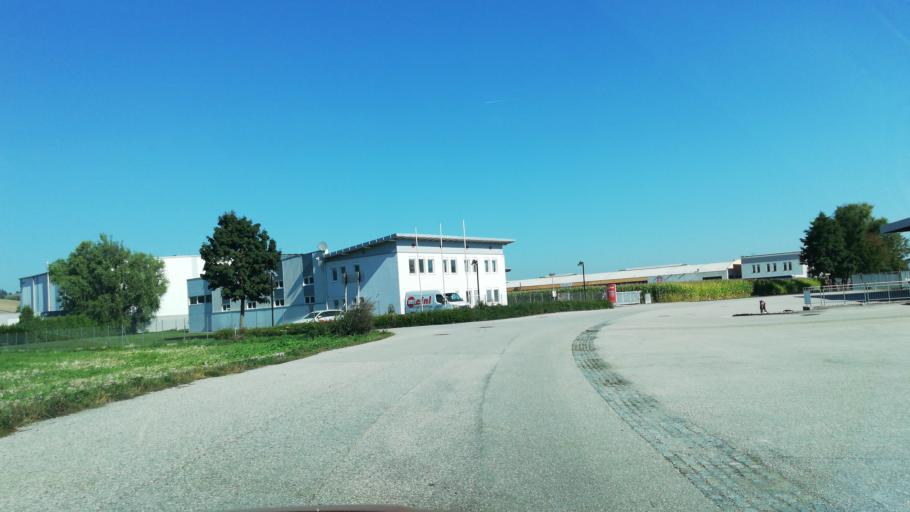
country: AT
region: Upper Austria
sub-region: Politischer Bezirk Grieskirchen
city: Bad Schallerbach
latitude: 48.2017
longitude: 13.9237
